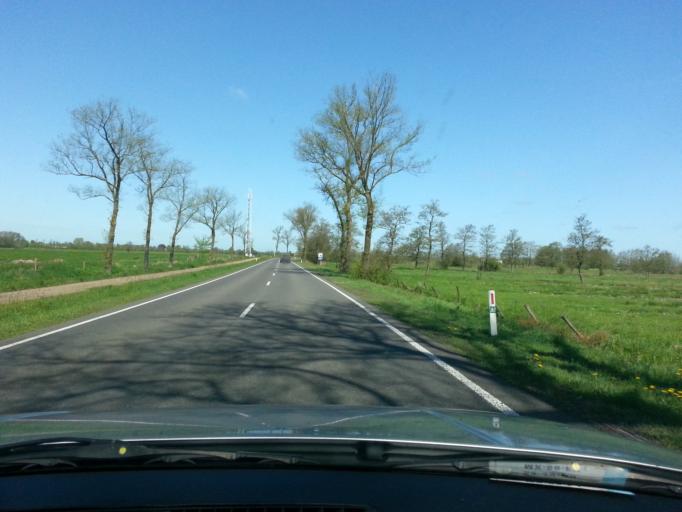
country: NL
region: Friesland
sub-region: Gemeente Achtkarspelen
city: Surhuizum
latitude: 53.2145
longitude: 6.1815
